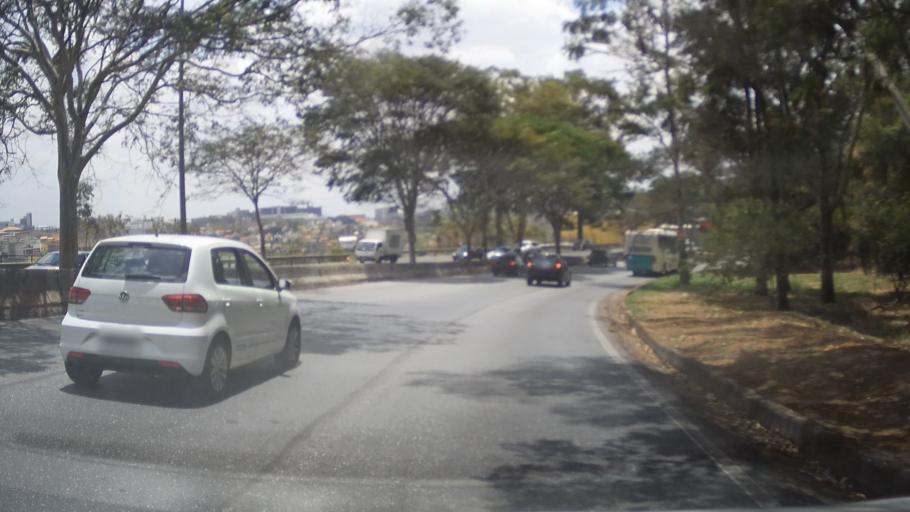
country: BR
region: Minas Gerais
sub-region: Belo Horizonte
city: Belo Horizonte
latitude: -19.9624
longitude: -43.9439
